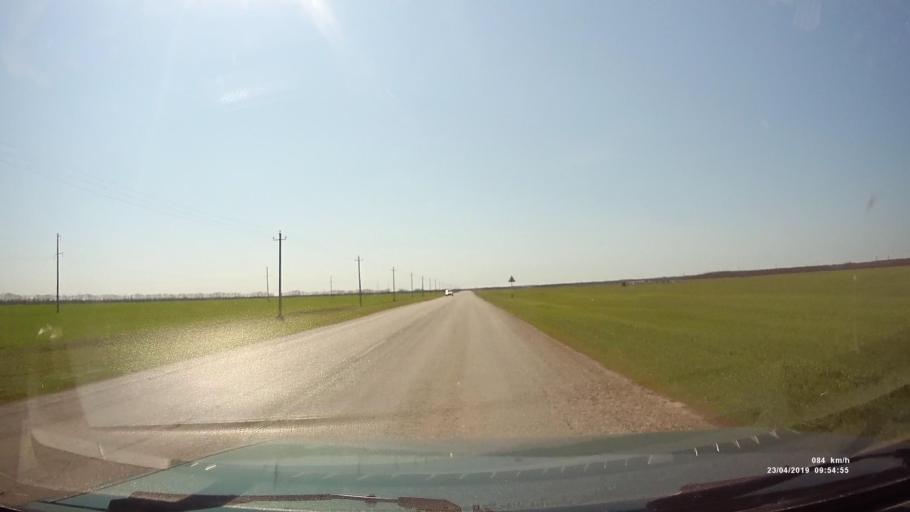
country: RU
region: Rostov
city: Orlovskiy
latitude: 46.8152
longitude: 42.0588
